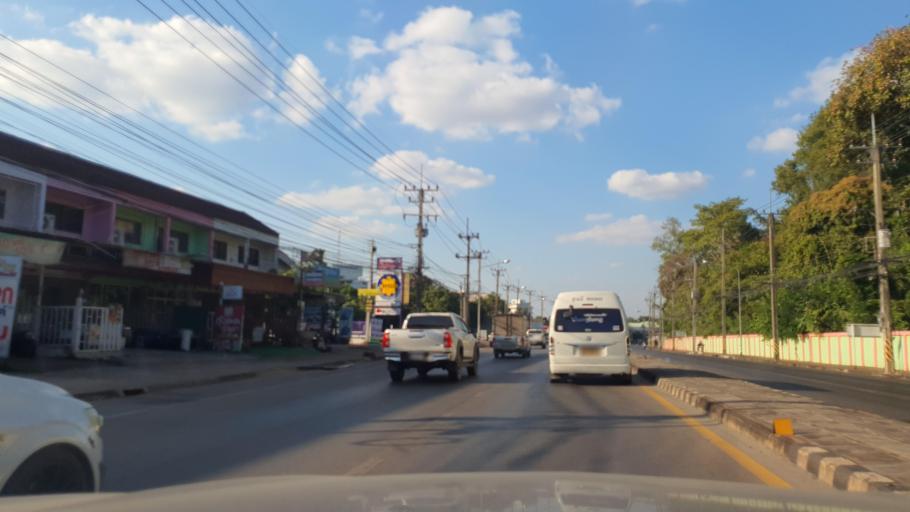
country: TH
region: Sakon Nakhon
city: Sakon Nakhon
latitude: 17.1845
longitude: 104.0936
